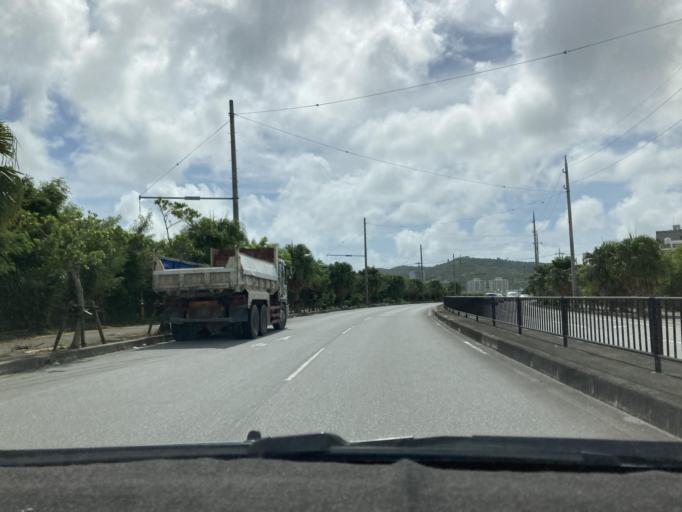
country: JP
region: Okinawa
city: Ginowan
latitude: 26.2107
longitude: 127.7645
